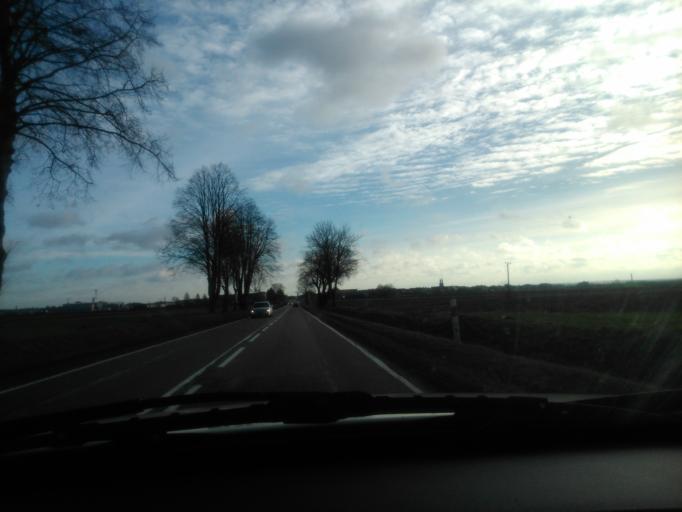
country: PL
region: Podlasie
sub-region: Powiat kolnenski
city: Kolno
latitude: 53.4164
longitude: 21.9036
